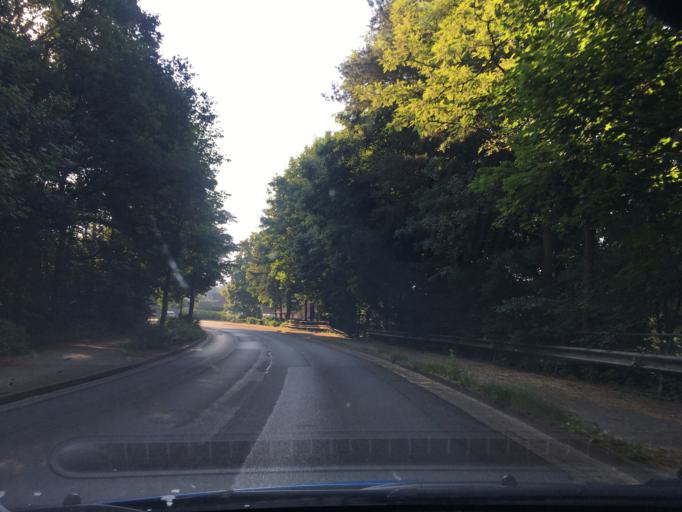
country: DE
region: Lower Saxony
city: Buchholz in der Nordheide
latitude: 53.3378
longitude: 9.8611
